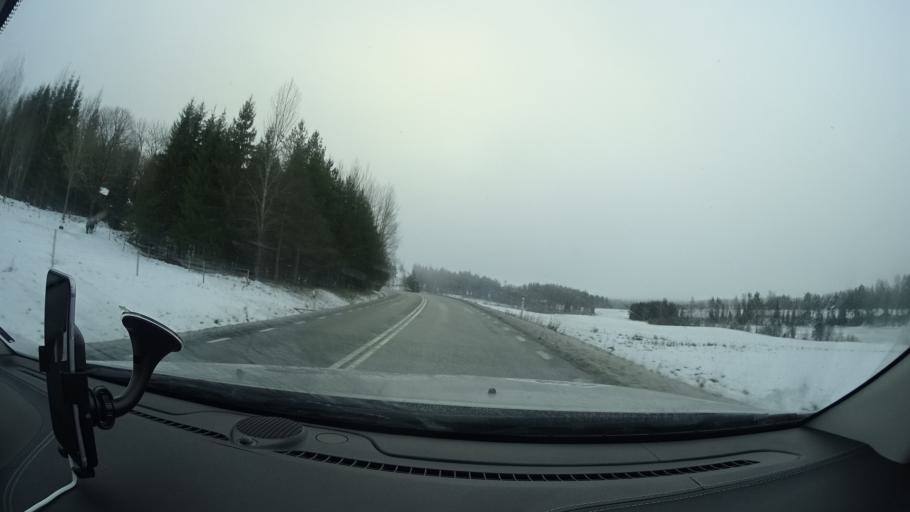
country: SE
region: OErebro
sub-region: Lindesbergs Kommun
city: Stora
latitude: 59.8292
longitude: 15.1115
